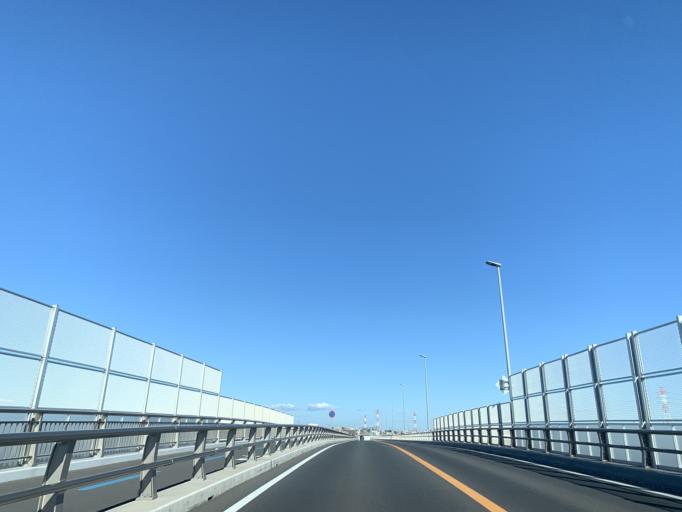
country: JP
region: Tokyo
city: Urayasu
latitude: 35.6903
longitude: 139.9336
